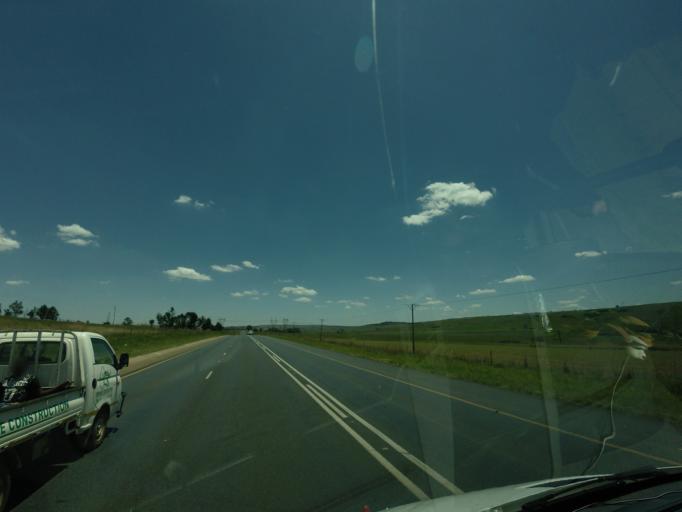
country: ZA
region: Mpumalanga
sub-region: Nkangala District Municipality
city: Belfast
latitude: -25.6780
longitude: 30.2279
